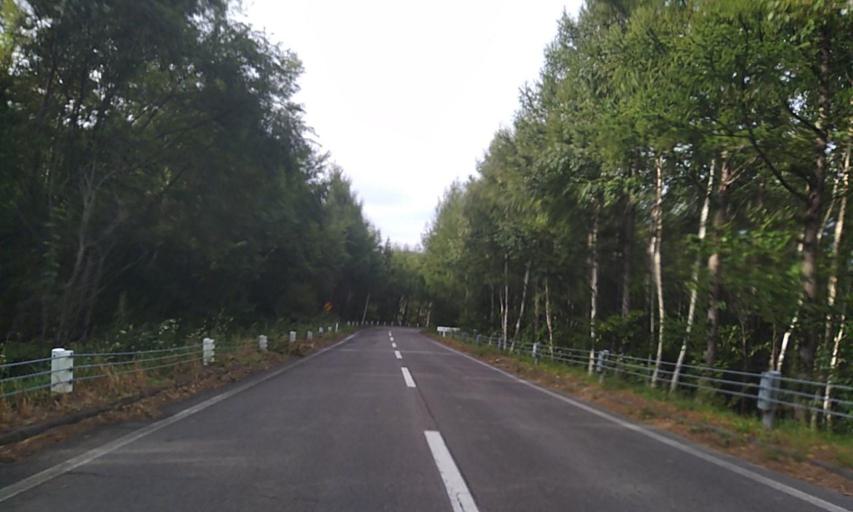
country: JP
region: Hokkaido
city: Abashiri
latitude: 43.7966
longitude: 144.5700
